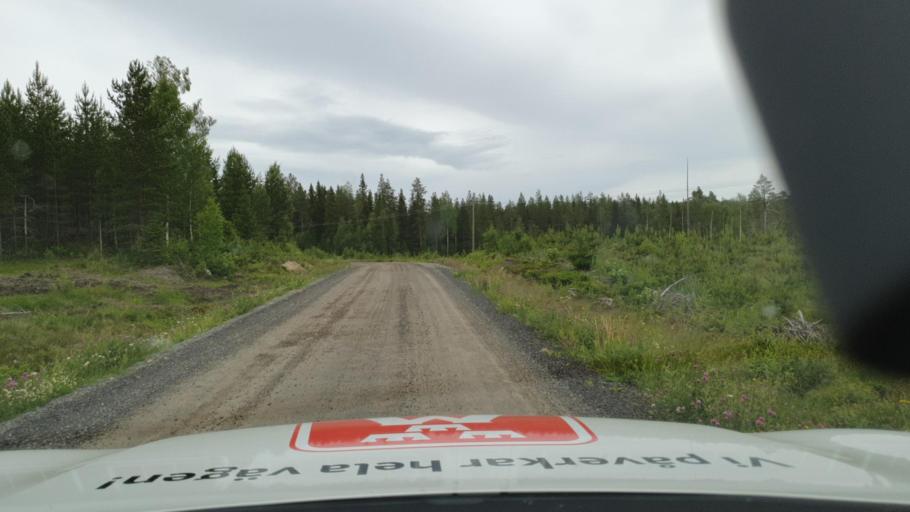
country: SE
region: Vaesterbotten
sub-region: Skelleftea Kommun
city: Burtraesk
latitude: 64.3560
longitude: 20.6155
